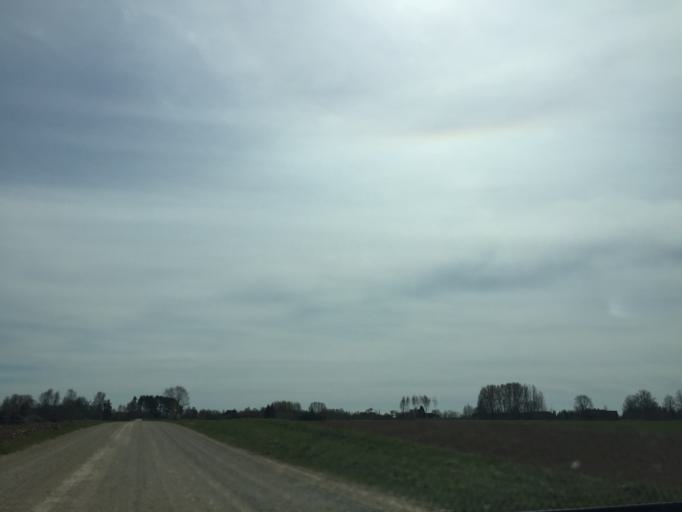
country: LV
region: Ludzas Rajons
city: Ludza
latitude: 56.5689
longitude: 27.5536
